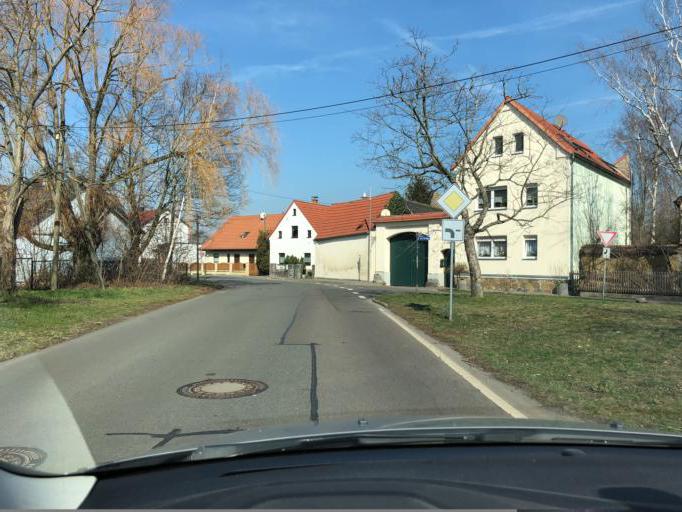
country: DE
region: Saxony
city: Rackwitz
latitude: 51.4221
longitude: 12.4209
